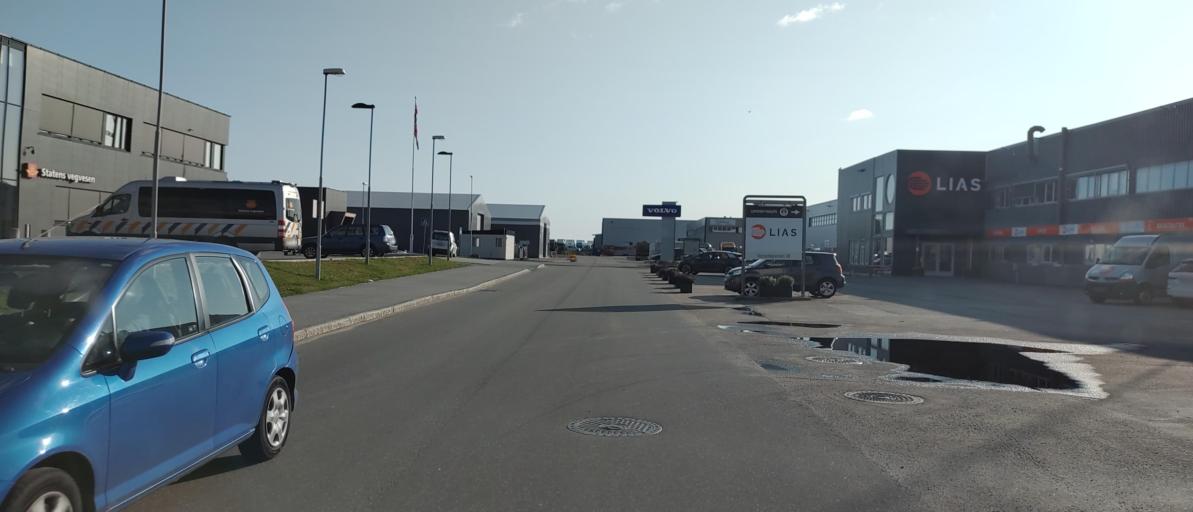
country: NO
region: Nordland
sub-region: Vagan
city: Svolvaer
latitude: 68.2292
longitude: 14.5579
